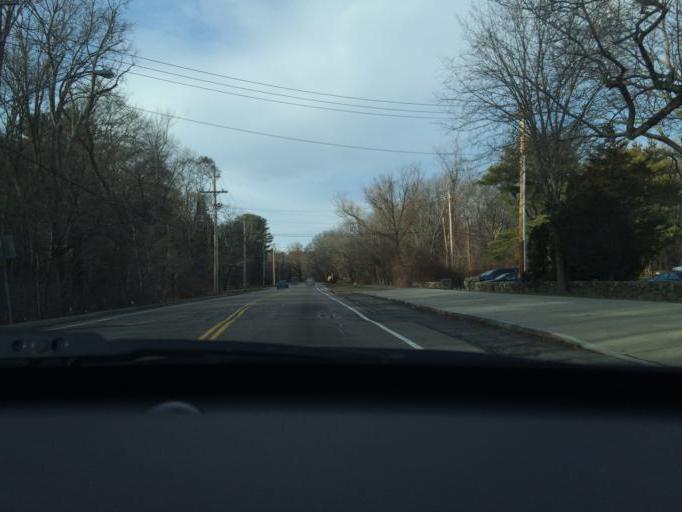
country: US
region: Massachusetts
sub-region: Norfolk County
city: Milton
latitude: 42.2585
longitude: -71.0601
